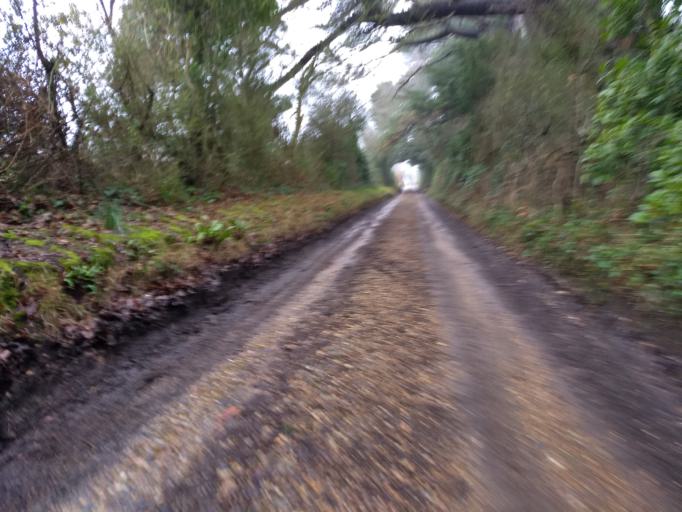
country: GB
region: England
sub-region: Isle of Wight
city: Newport
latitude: 50.7169
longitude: -1.2419
